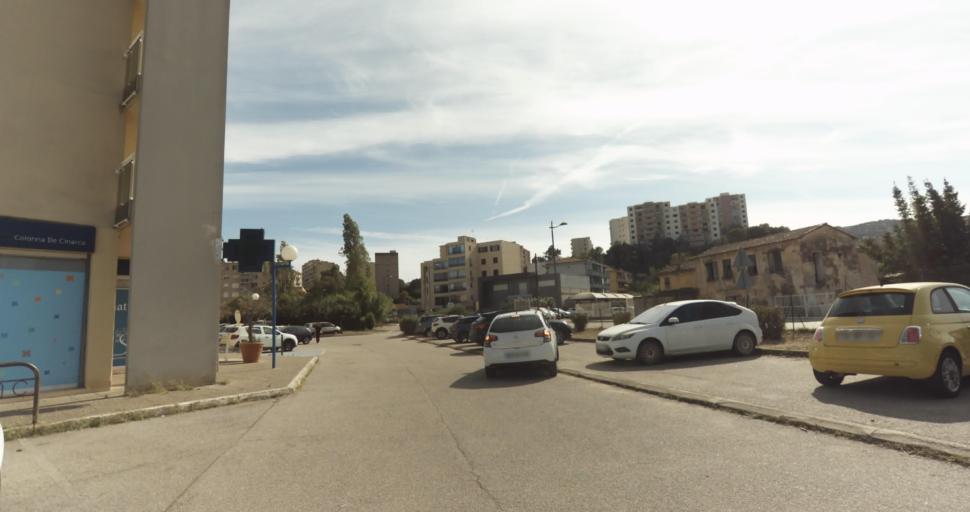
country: FR
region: Corsica
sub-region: Departement de la Corse-du-Sud
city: Ajaccio
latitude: 41.9364
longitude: 8.7361
